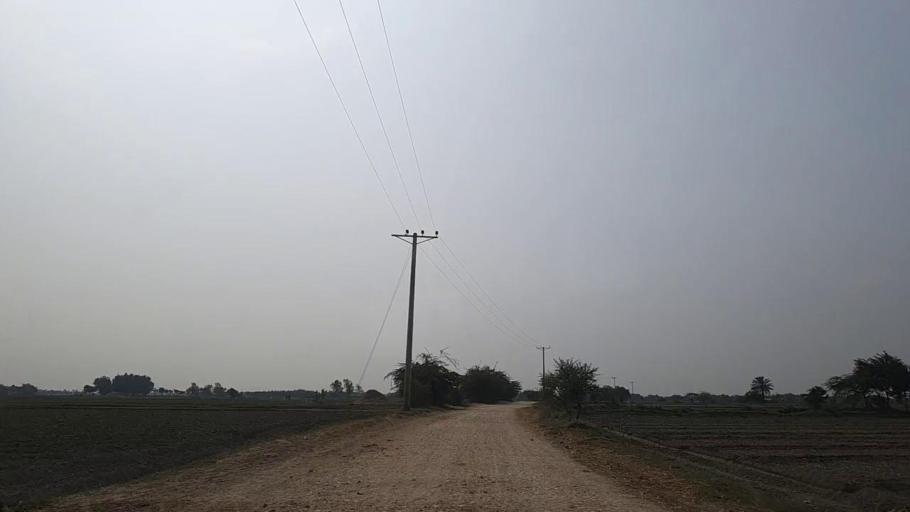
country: PK
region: Sindh
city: Mirpur Sakro
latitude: 24.6147
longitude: 67.7317
